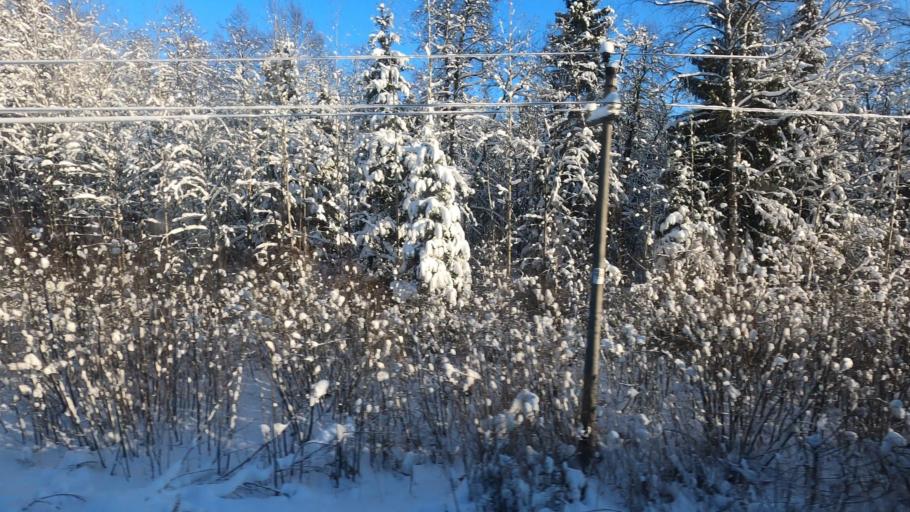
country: RU
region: Moskovskaya
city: Novo-Nikol'skoye
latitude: 56.6270
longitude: 37.5642
